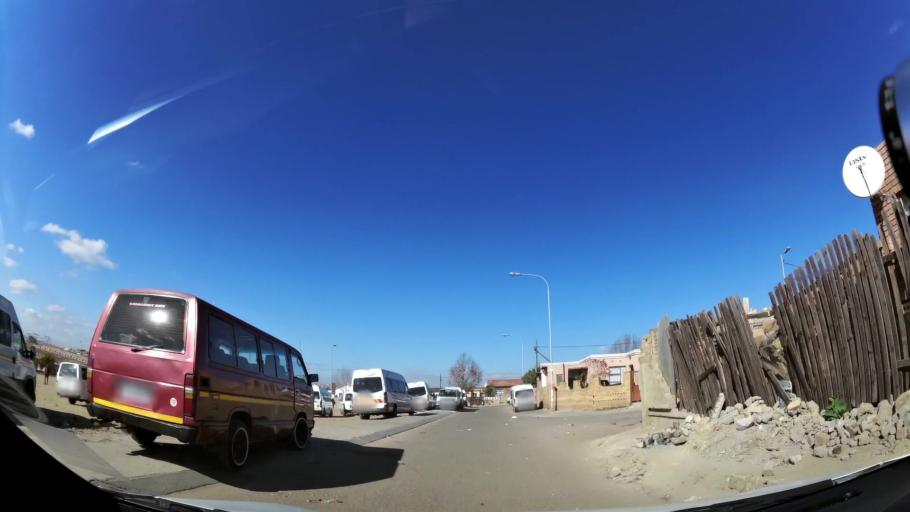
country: ZA
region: Gauteng
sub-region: City of Johannesburg Metropolitan Municipality
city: Midrand
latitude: -25.9144
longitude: 28.0943
